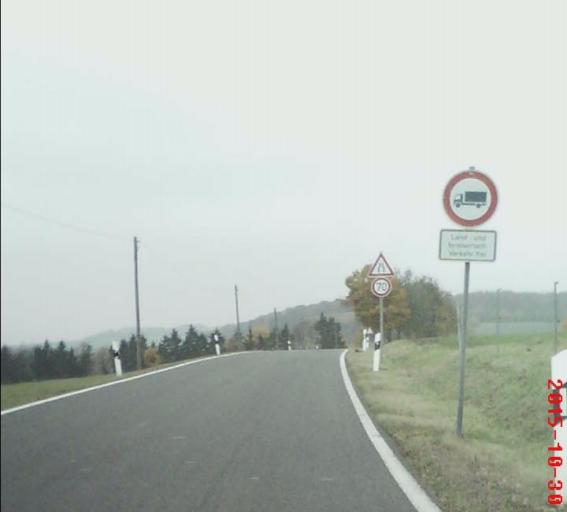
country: DE
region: Thuringia
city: Wachstedt
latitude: 51.3024
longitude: 10.2265
